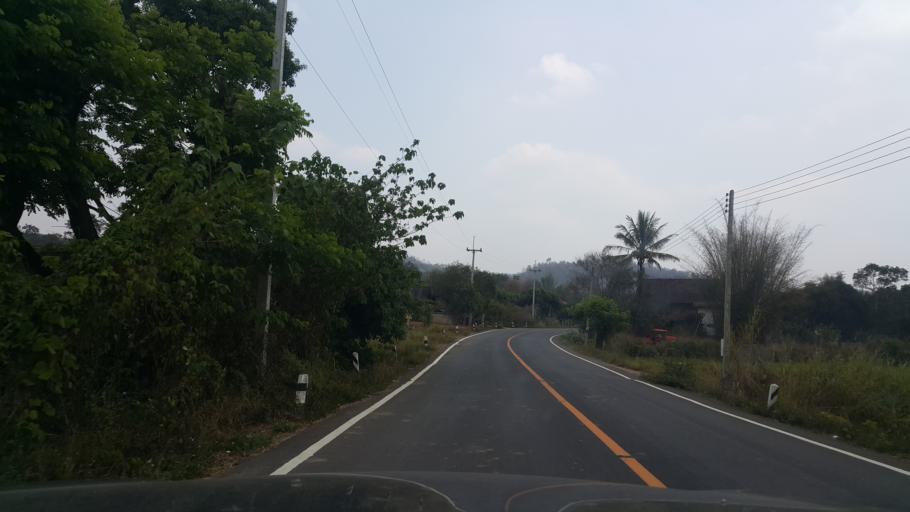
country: TH
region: Lamphun
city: Thung Hua Chang
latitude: 18.1384
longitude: 99.0082
